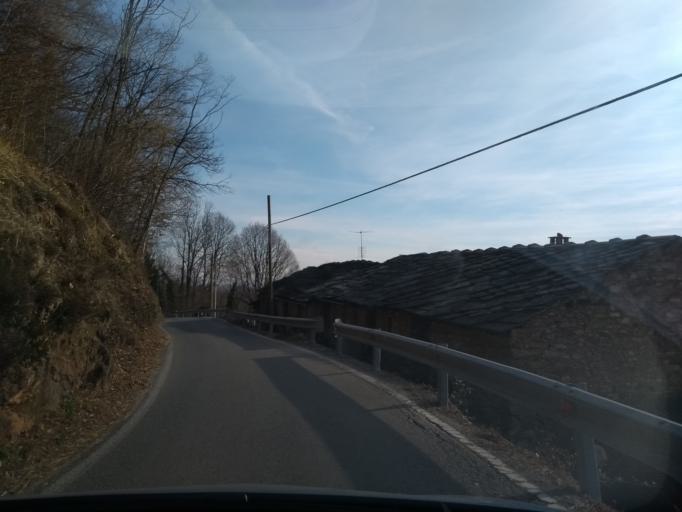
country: IT
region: Piedmont
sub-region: Provincia di Torino
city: Lanzo Torinese
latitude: 45.2901
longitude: 7.4994
